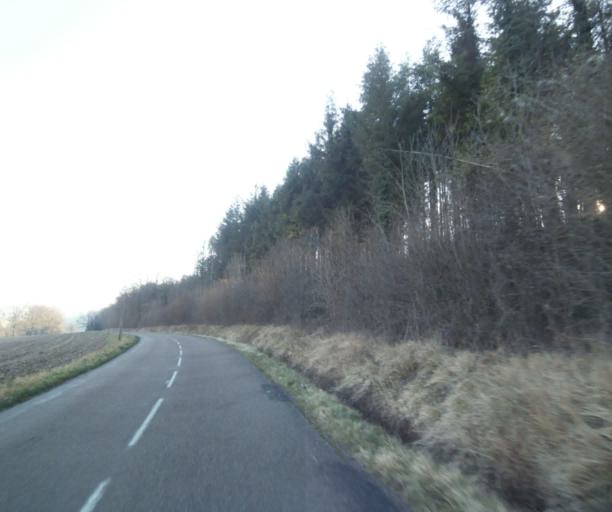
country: FR
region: Champagne-Ardenne
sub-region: Departement de la Haute-Marne
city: Bienville
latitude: 48.5608
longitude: 5.0828
